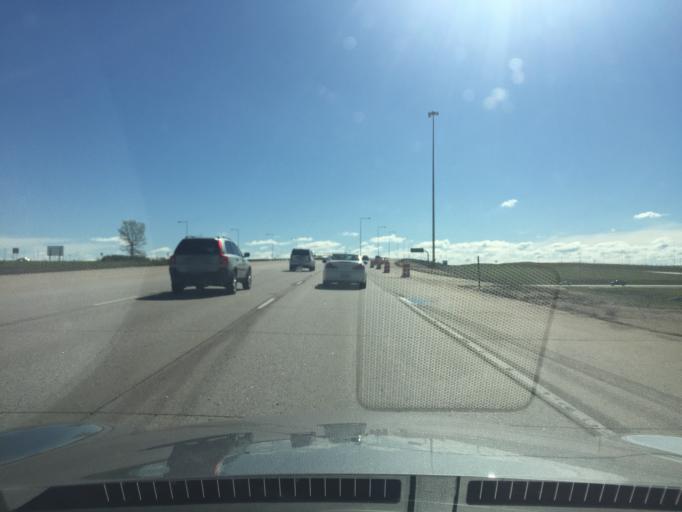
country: US
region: Colorado
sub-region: Adams County
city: Aurora
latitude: 39.8335
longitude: -104.7184
